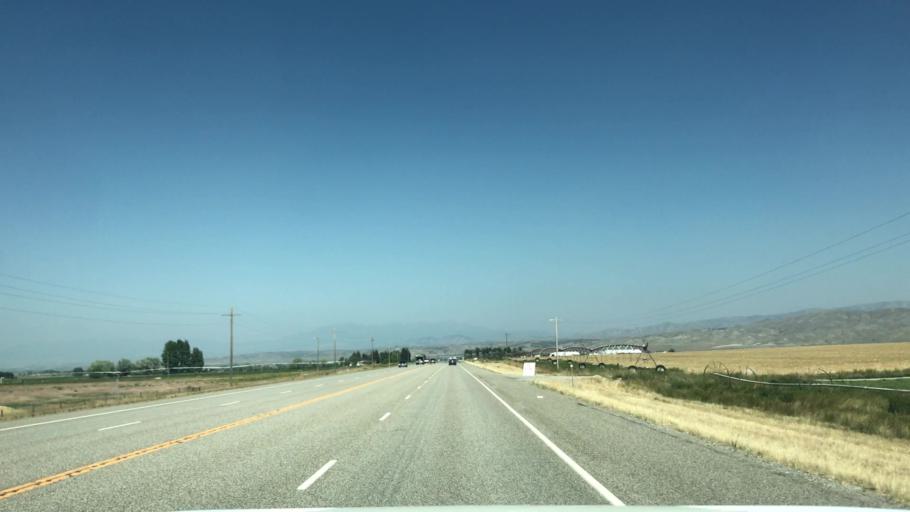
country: US
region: Montana
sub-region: Broadwater County
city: Townsend
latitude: 46.1308
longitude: -111.4873
